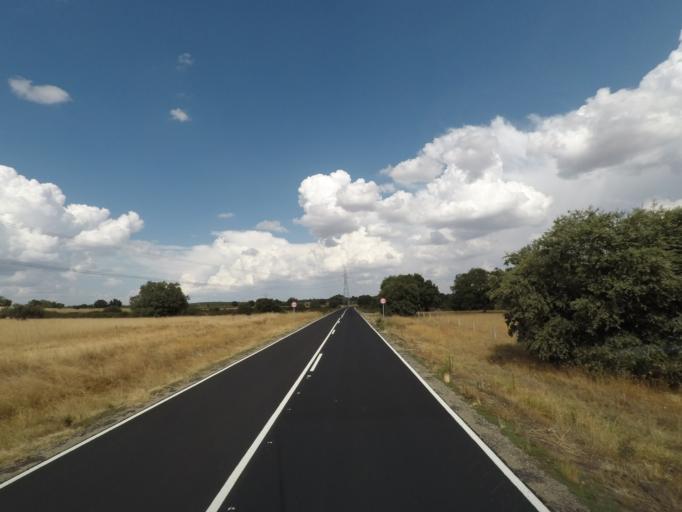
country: ES
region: Castille and Leon
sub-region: Provincia de Zamora
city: Fermoselle
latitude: 41.3001
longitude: -6.3269
